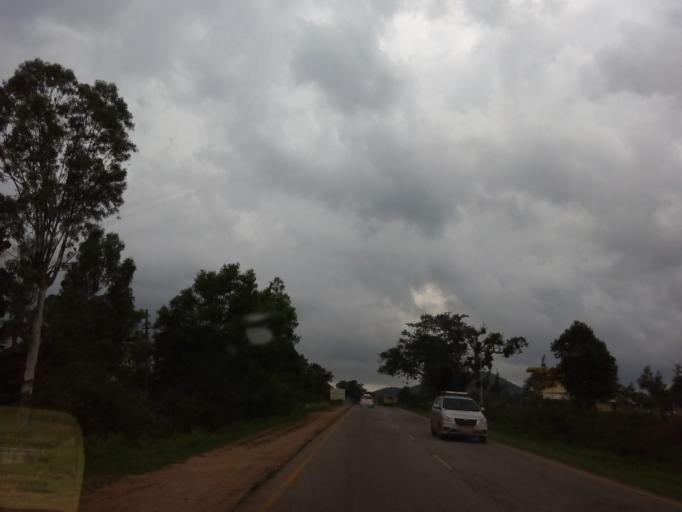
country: IN
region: Karnataka
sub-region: Hassan
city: Hassan
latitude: 13.0782
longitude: 76.0457
